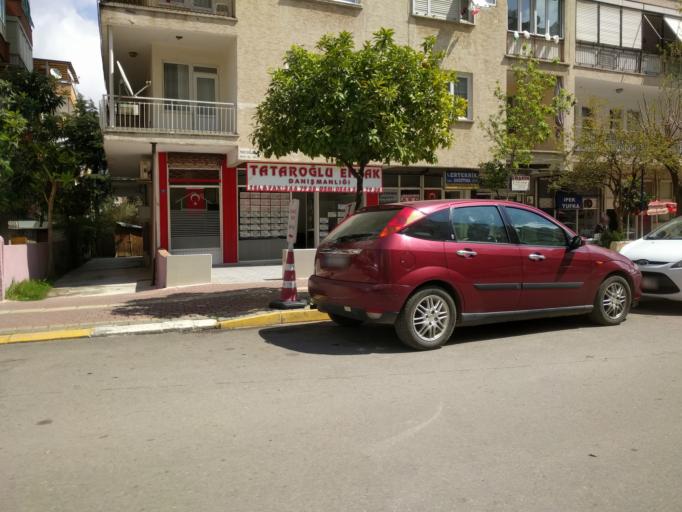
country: TR
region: Antalya
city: Antalya
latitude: 36.9100
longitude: 30.6829
